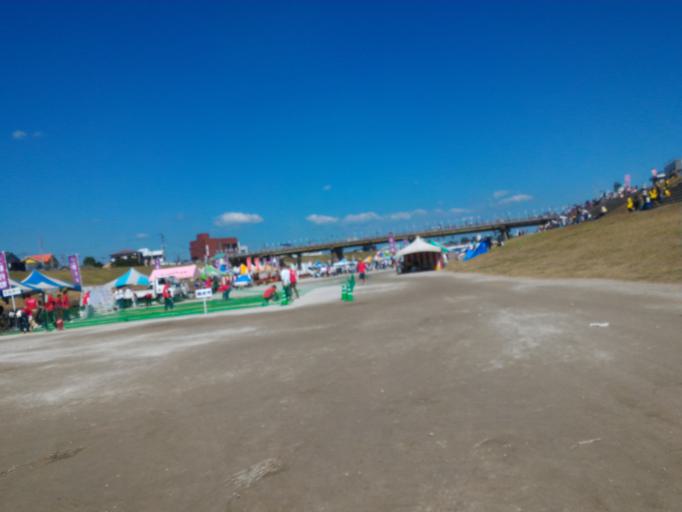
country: JP
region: Kagoshima
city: Kanoya
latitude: 31.3451
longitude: 130.9423
